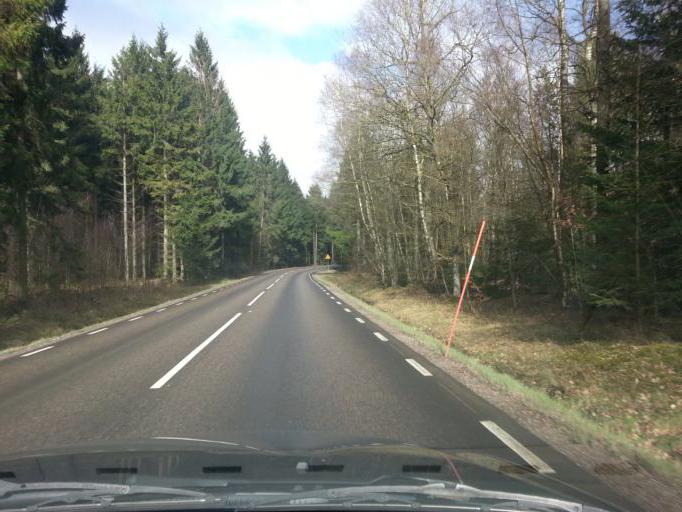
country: SE
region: Skane
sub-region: Astorps Kommun
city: Astorp
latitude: 56.1170
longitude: 12.9909
